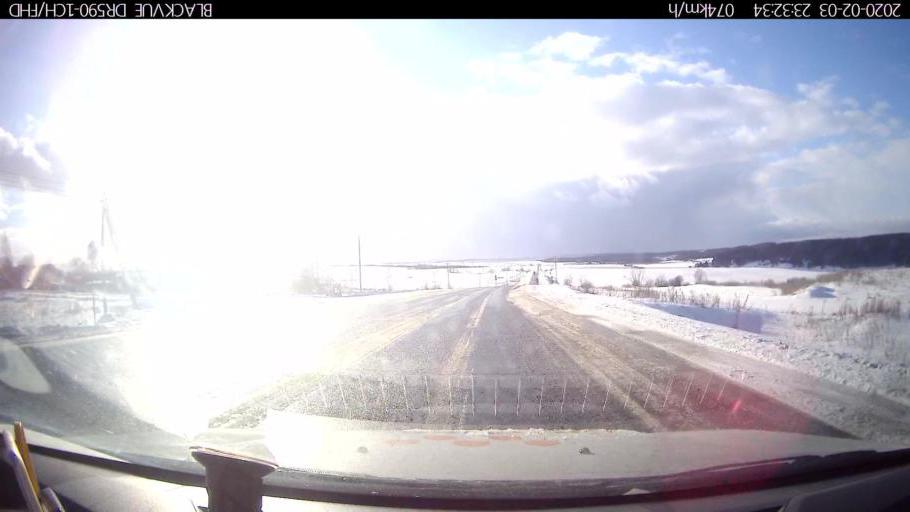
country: RU
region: Nizjnij Novgorod
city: Dal'neye Konstantinovo
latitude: 55.9305
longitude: 44.2253
